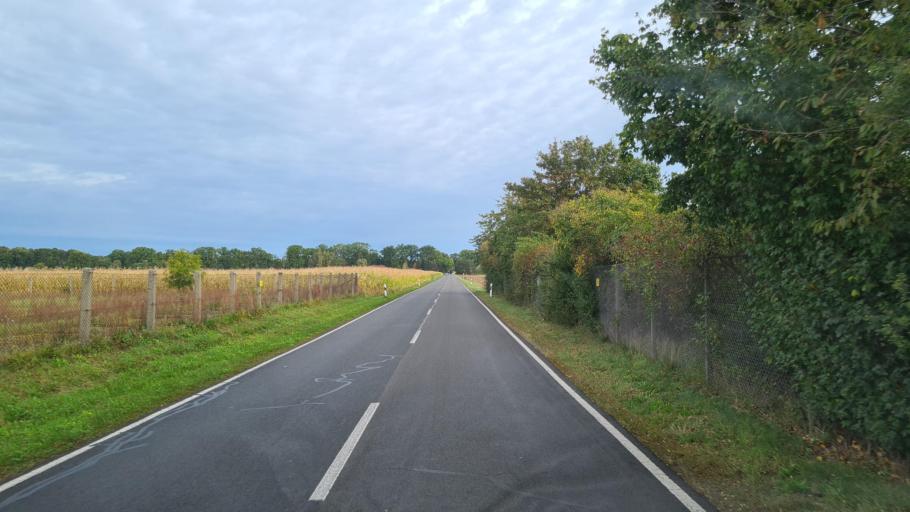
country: DE
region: Brandenburg
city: Kasel-Golzig
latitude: 51.9284
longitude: 13.7077
